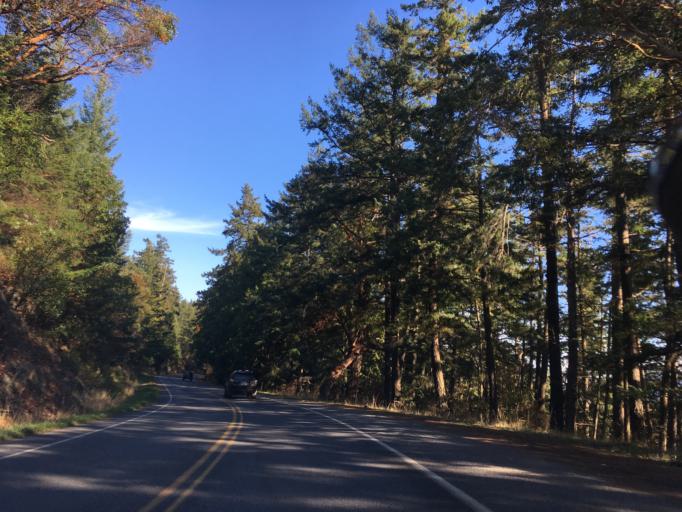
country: US
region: Washington
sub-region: San Juan County
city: Friday Harbor
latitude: 48.6886
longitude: -122.9228
